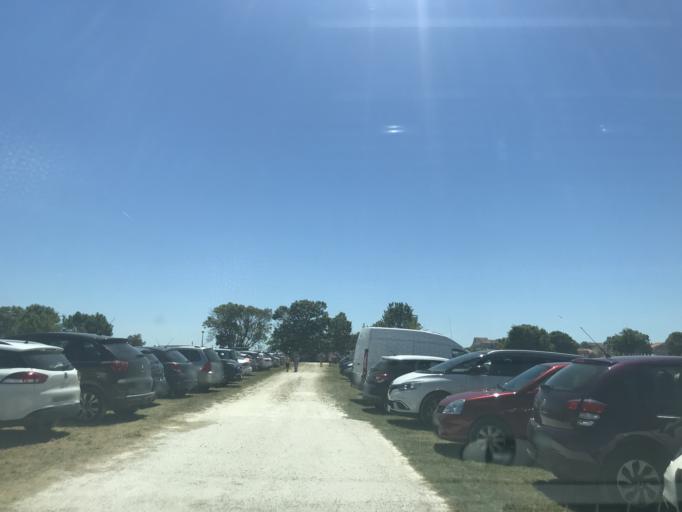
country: FR
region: Poitou-Charentes
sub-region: Departement de la Charente-Maritime
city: Meschers-sur-Gironde
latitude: 45.5367
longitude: -0.9037
